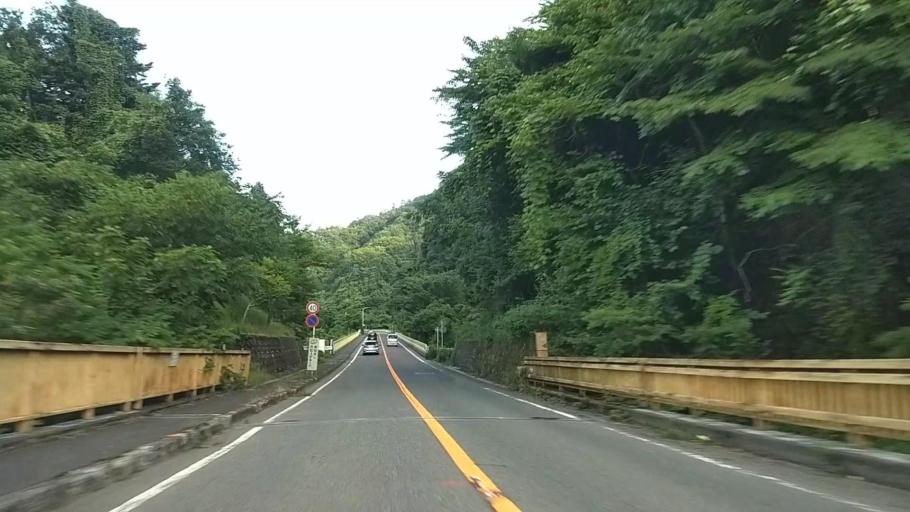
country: JP
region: Yamanashi
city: Uenohara
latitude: 35.5205
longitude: 139.2254
